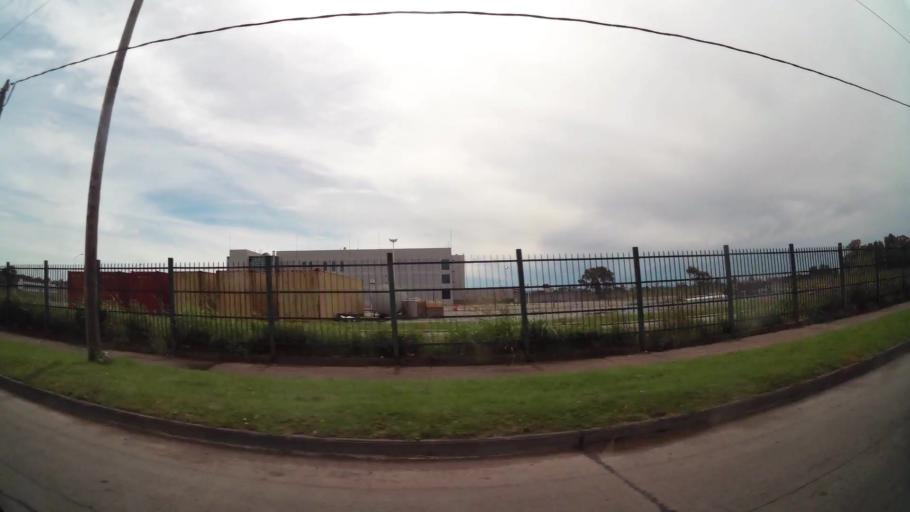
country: AR
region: Buenos Aires F.D.
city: Villa Lugano
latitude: -34.6717
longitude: -58.4576
